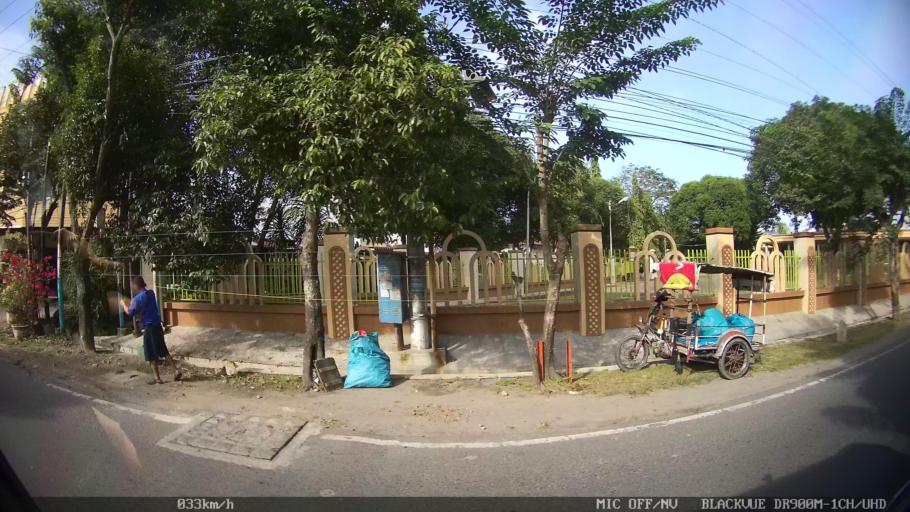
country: ID
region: North Sumatra
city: Medan
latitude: 3.6037
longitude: 98.6592
